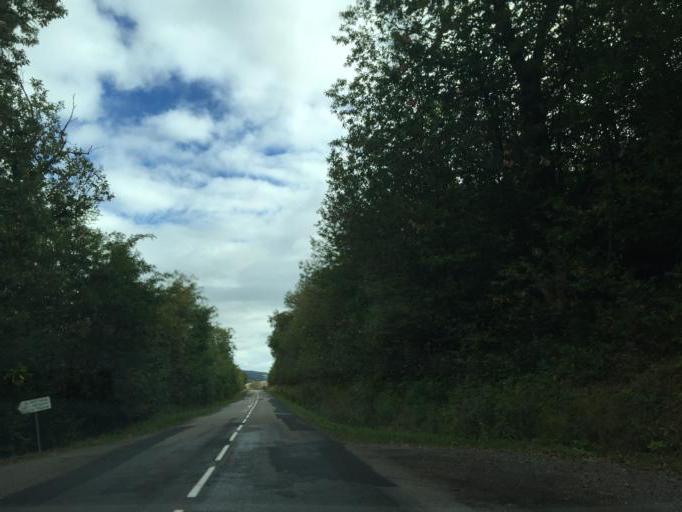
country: FR
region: Rhone-Alpes
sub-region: Departement de la Loire
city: Pelussin
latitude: 45.4612
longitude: 4.6456
